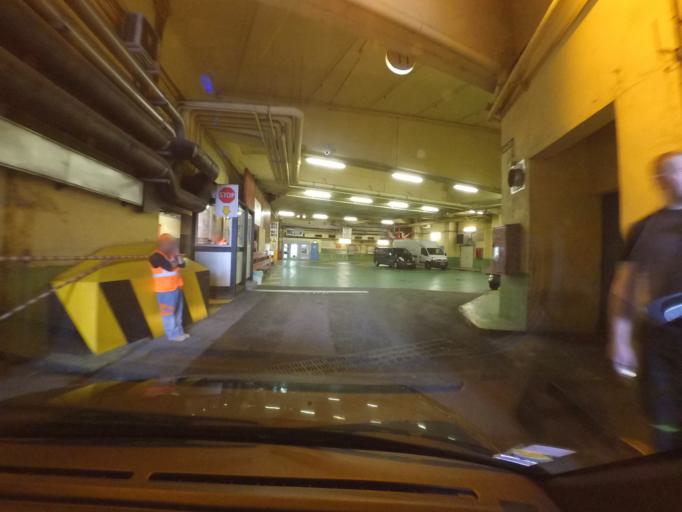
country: FR
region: Ile-de-France
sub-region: Departement des Hauts-de-Seine
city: Levallois-Perret
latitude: 48.8799
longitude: 2.2848
